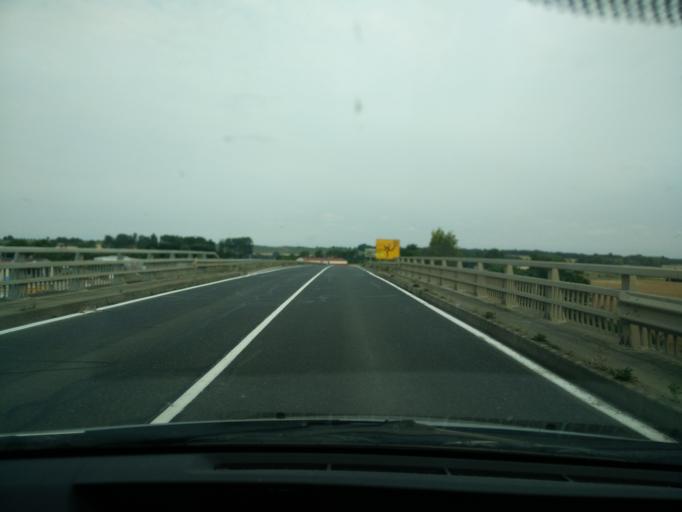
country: FR
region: Poitou-Charentes
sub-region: Departement des Deux-Sevres
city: Louzy
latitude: 47.0105
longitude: -0.1971
